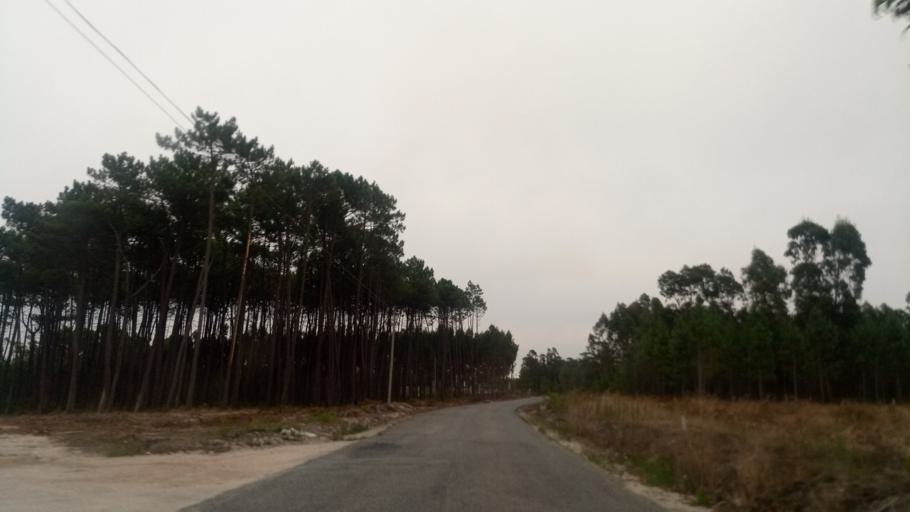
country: PT
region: Leiria
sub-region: Caldas da Rainha
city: Caldas da Rainha
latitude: 39.4460
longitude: -9.1680
